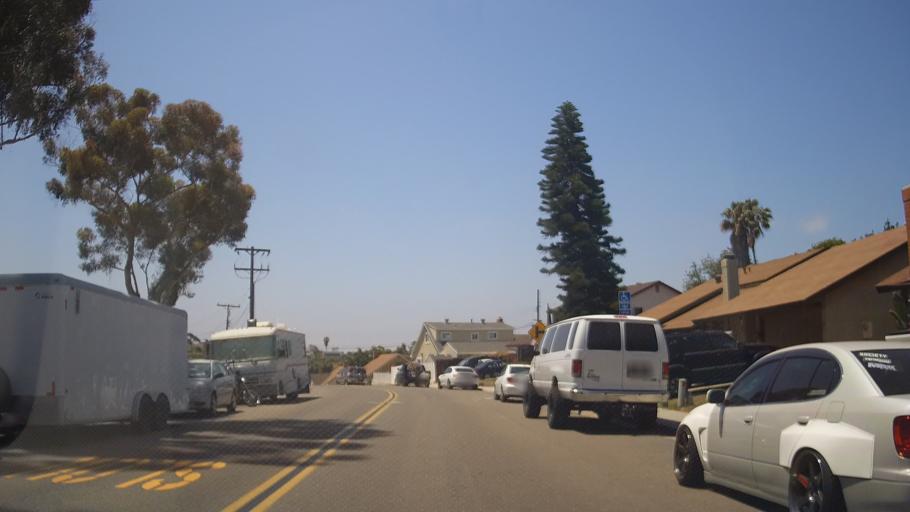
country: US
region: California
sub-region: San Diego County
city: Bonita
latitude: 32.6737
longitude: -117.0483
